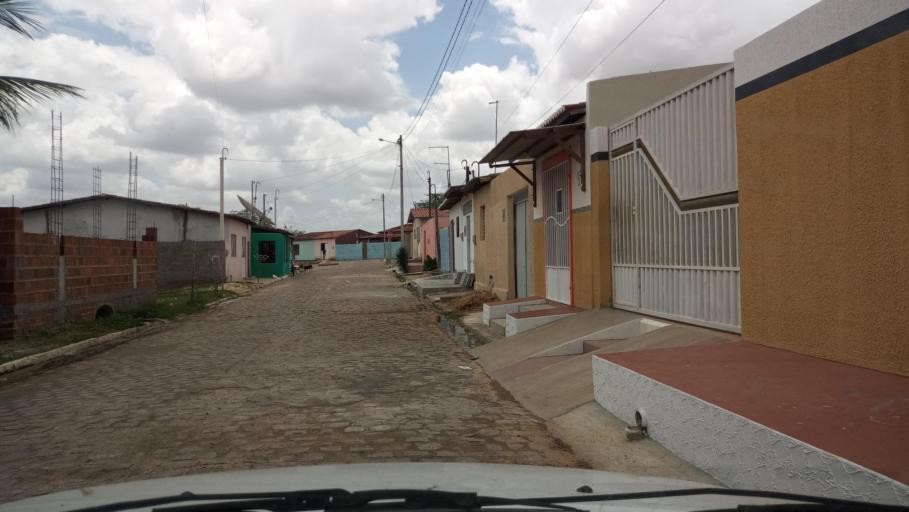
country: BR
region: Rio Grande do Norte
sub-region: Tangara
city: Tangara
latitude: -6.1009
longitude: -35.7125
